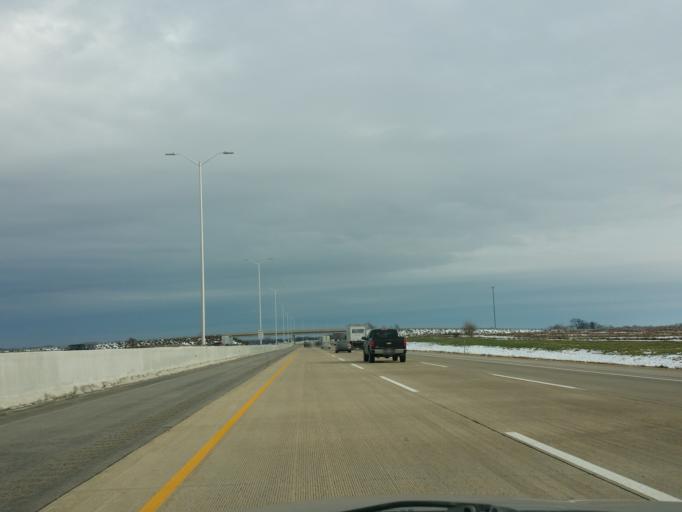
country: US
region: Illinois
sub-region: Boone County
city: Belvidere
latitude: 42.2338
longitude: -88.7937
